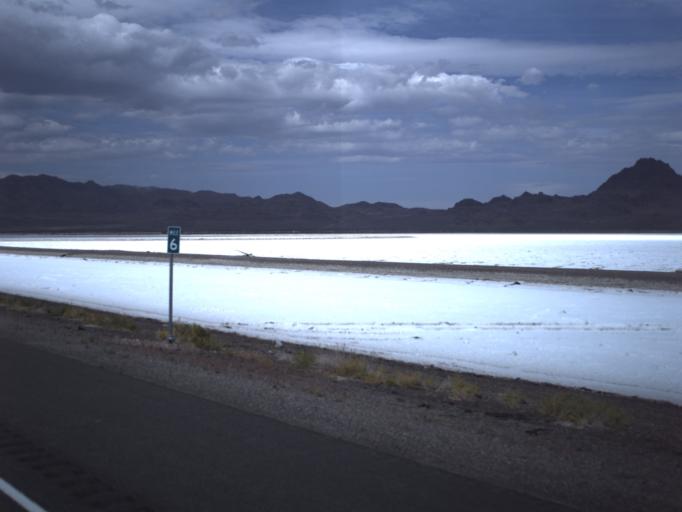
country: US
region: Utah
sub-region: Tooele County
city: Wendover
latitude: 40.7410
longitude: -113.9319
